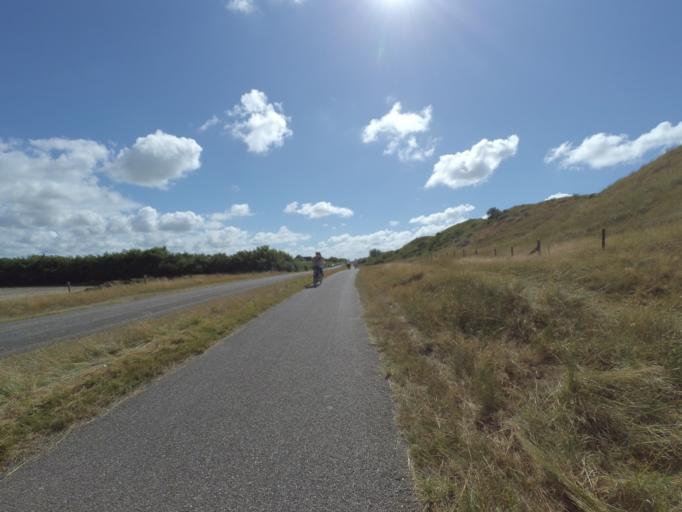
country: NL
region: North Holland
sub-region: Gemeente Texel
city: Den Burg
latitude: 53.1292
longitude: 4.8147
